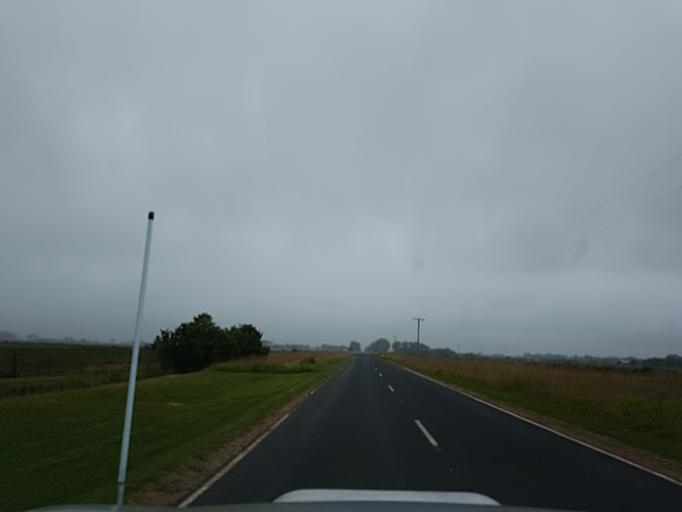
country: AU
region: Victoria
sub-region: Wellington
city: Sale
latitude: -38.0648
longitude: 147.0487
